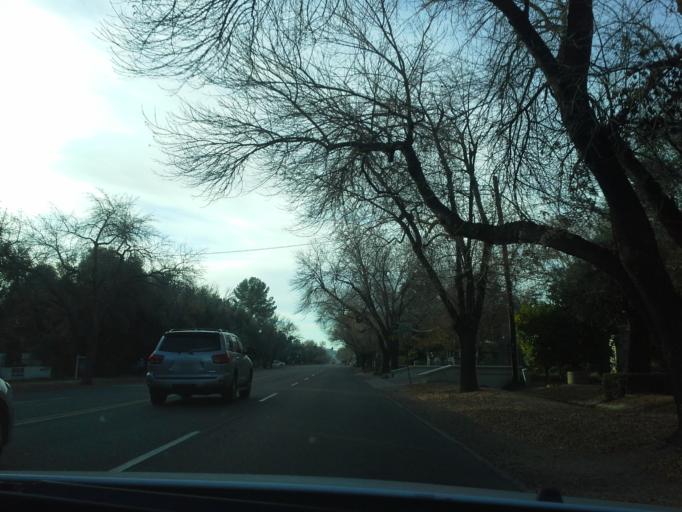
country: US
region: Arizona
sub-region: Maricopa County
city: Phoenix
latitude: 33.5333
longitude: -112.0738
